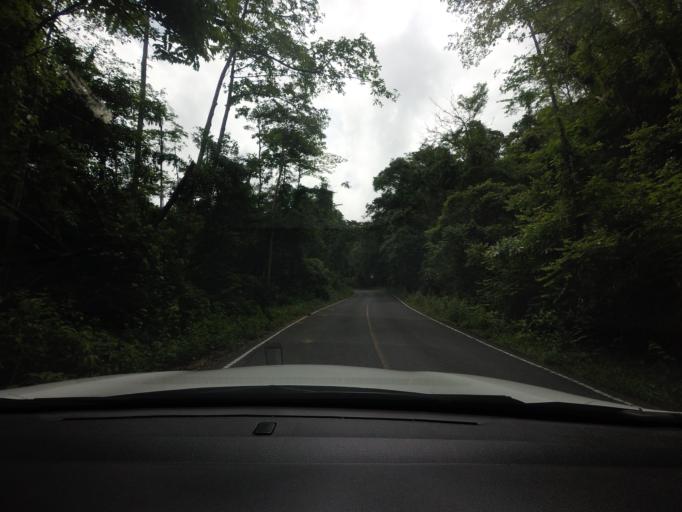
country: TH
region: Nakhon Nayok
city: Pak Phli
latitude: 14.2632
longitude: 101.3866
